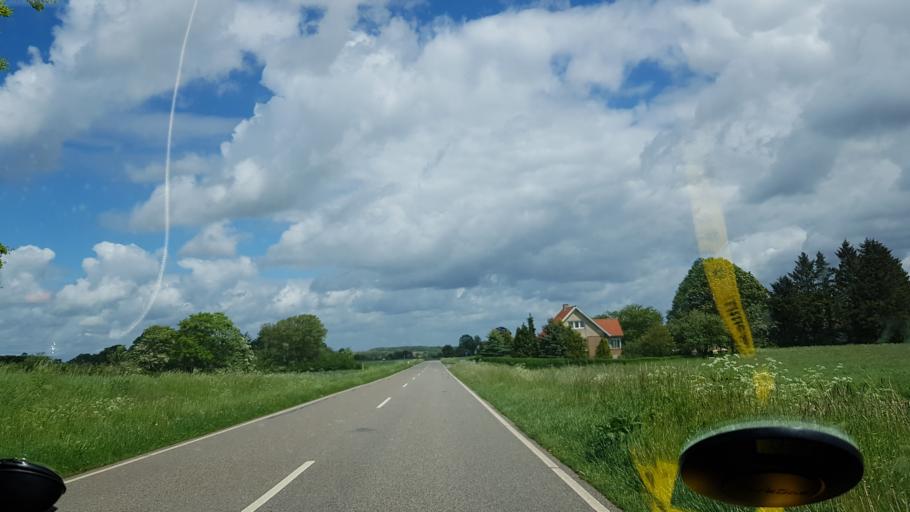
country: DK
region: South Denmark
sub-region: Kolding Kommune
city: Christiansfeld
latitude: 55.3396
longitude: 9.4624
